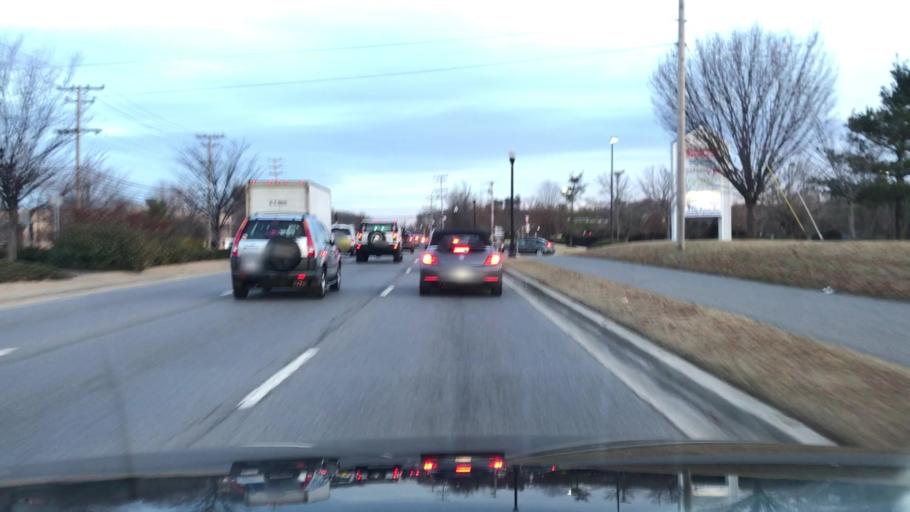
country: US
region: Maryland
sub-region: Anne Arundel County
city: Parole
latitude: 38.9708
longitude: -76.5221
